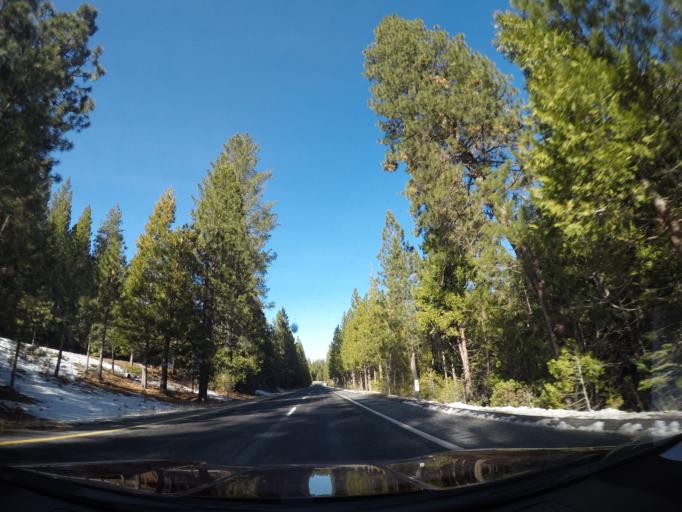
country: US
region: California
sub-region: Tuolumne County
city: Twain Harte
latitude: 38.1084
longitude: -120.1229
